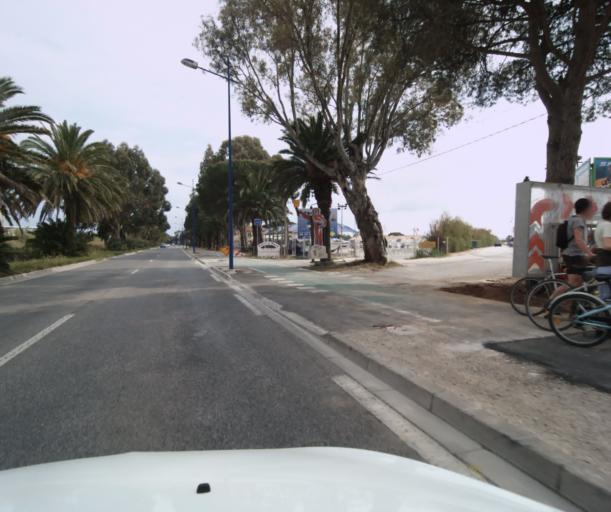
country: FR
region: Provence-Alpes-Cote d'Azur
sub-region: Departement du Var
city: Hyeres
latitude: 43.0898
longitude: 6.1438
